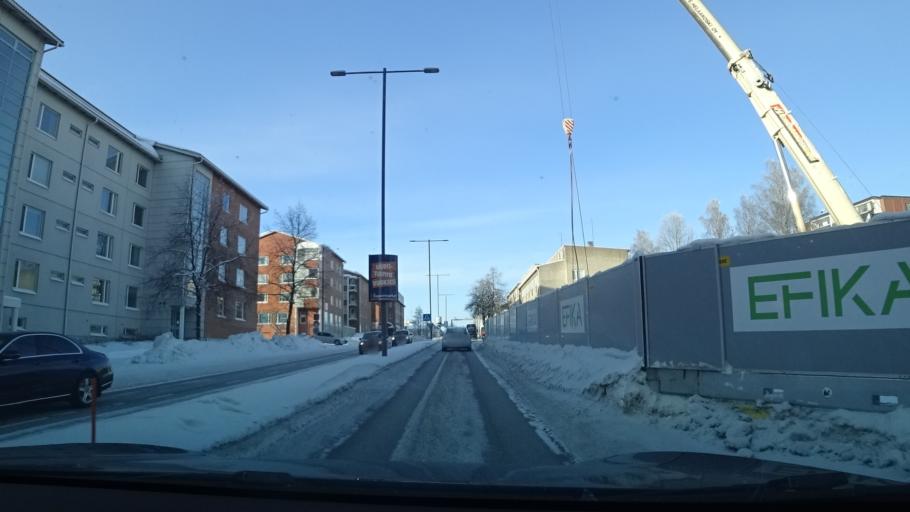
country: FI
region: South Karelia
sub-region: Lappeenranta
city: Lappeenranta
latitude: 61.0530
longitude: 28.1921
